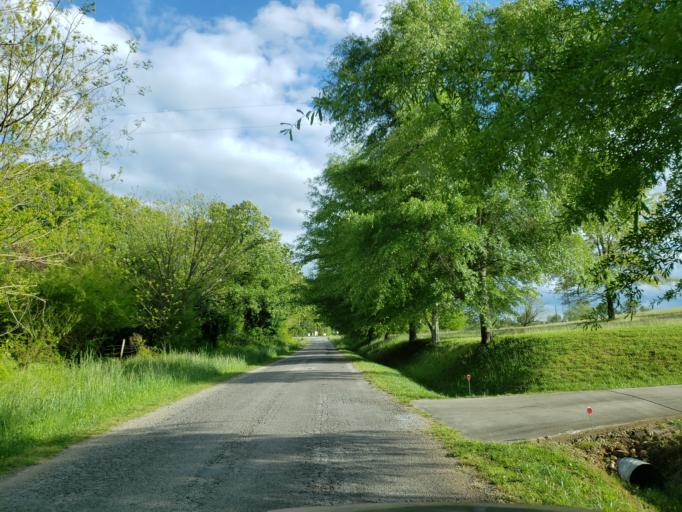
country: US
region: Georgia
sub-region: Haralson County
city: Tallapoosa
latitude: 33.8140
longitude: -85.2906
